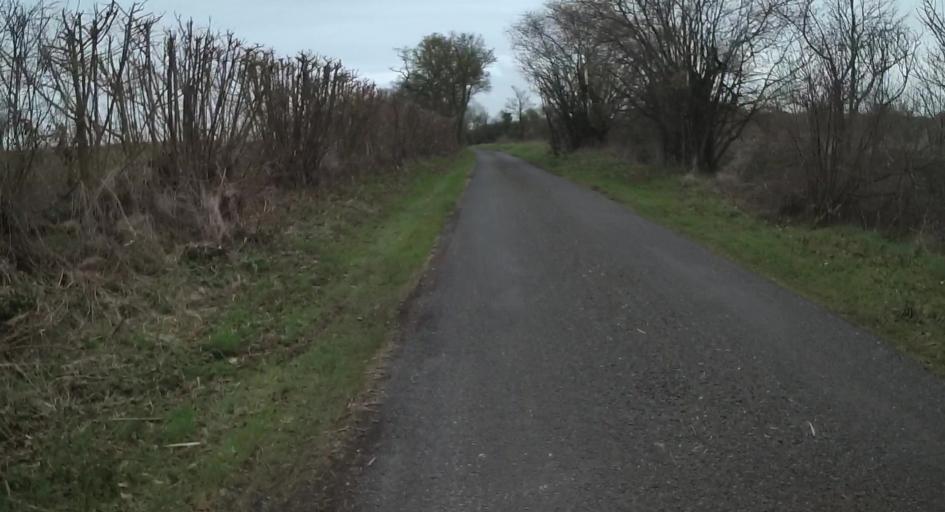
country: GB
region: England
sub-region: Hampshire
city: Overton
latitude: 51.2645
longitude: -1.2456
